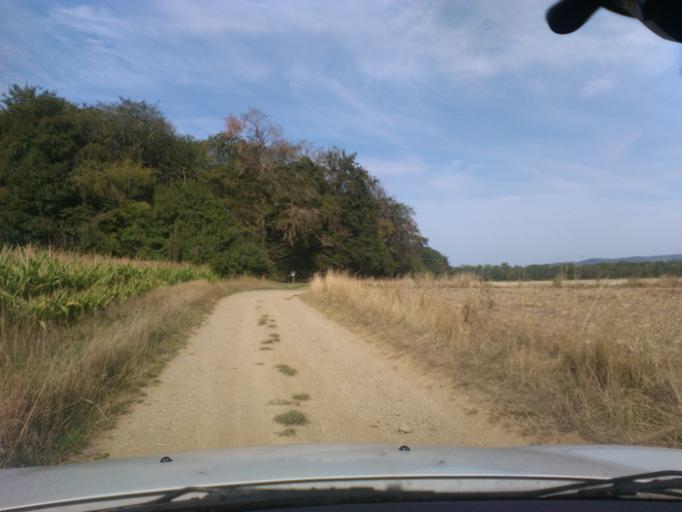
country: FR
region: Lorraine
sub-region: Departement des Vosges
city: Mirecourt
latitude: 48.3214
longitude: 6.0937
